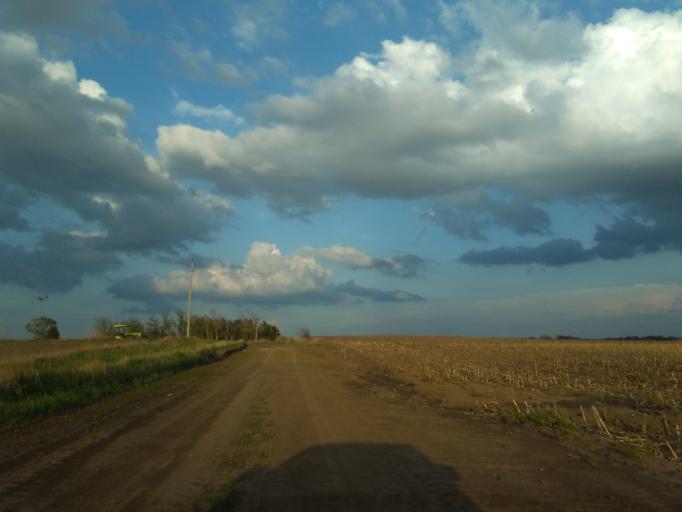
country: US
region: Nebraska
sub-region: Webster County
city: Red Cloud
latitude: 40.2054
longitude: -98.3975
